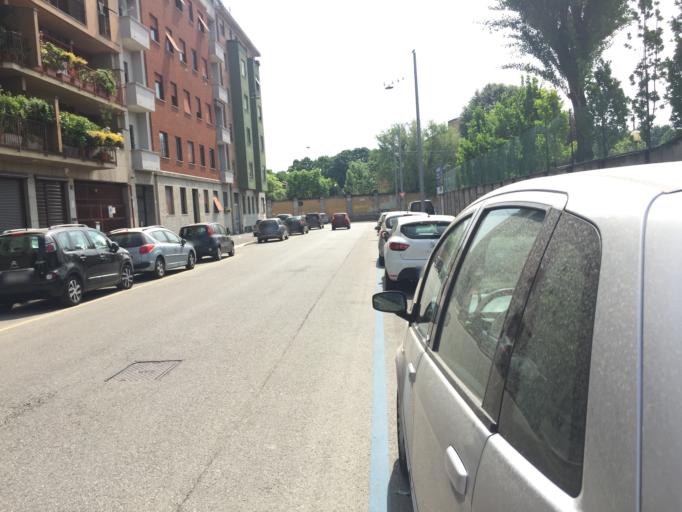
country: IT
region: Lombardy
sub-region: Citta metropolitana di Milano
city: Novate Milanese
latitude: 45.4918
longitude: 9.1562
